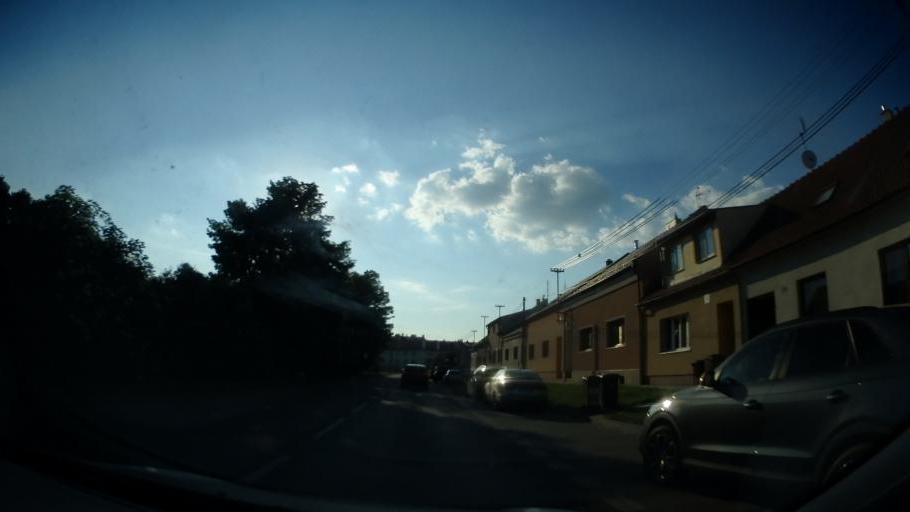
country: CZ
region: South Moravian
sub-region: Okres Vyskov
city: Vyskov
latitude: 49.2802
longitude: 17.0071
